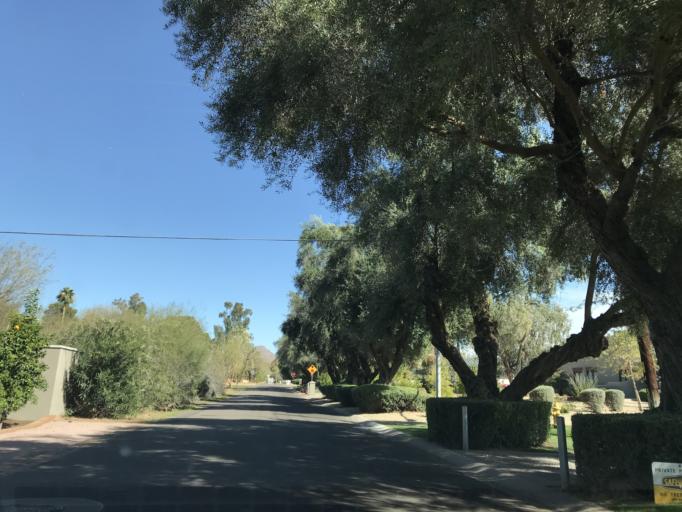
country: US
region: Arizona
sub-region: Maricopa County
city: Phoenix
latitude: 33.5130
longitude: -112.0358
